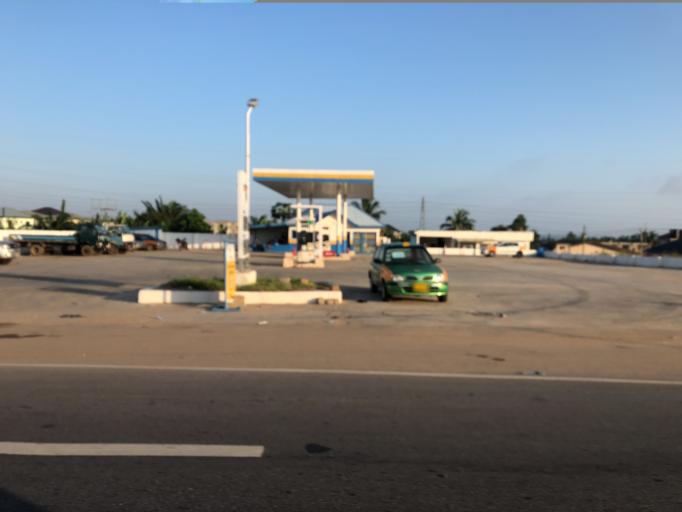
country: GH
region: Central
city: Kasoa
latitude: 5.5294
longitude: -0.4481
